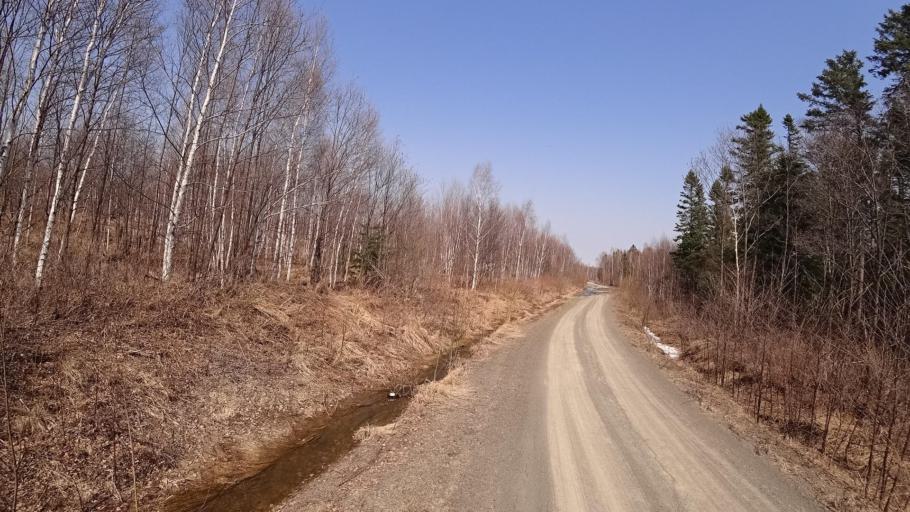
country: RU
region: Khabarovsk Krai
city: Selikhino
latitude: 50.6200
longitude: 137.3931
